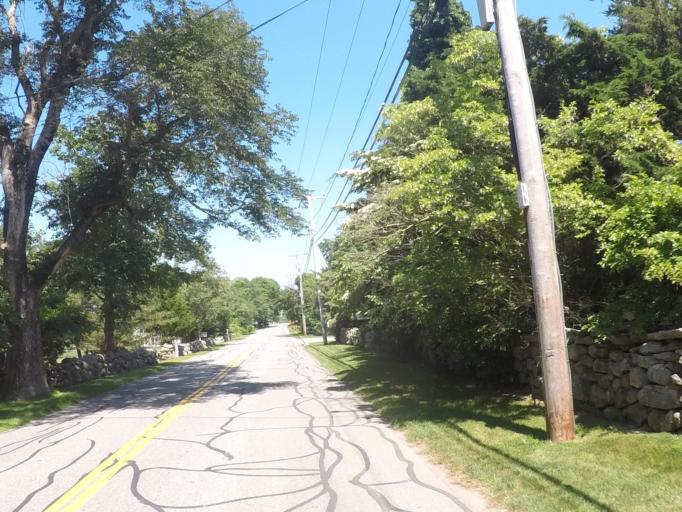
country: US
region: Massachusetts
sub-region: Bristol County
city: Bliss Corner
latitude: 41.5390
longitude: -70.9521
